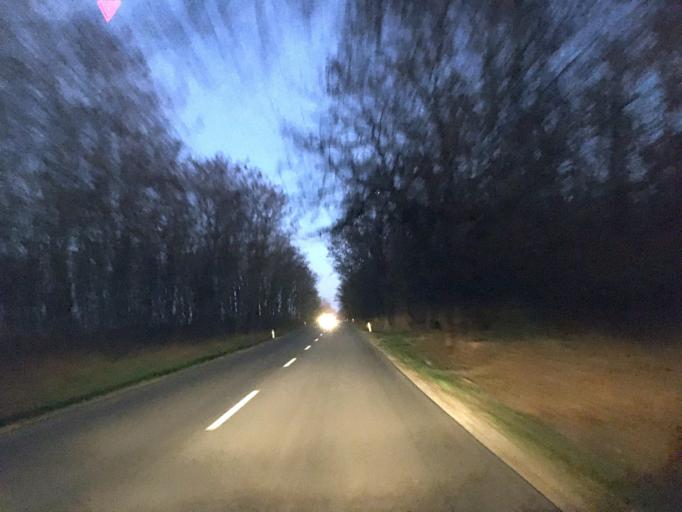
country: SK
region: Nitriansky
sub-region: Okres Komarno
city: Hurbanovo
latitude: 47.8979
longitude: 18.1638
